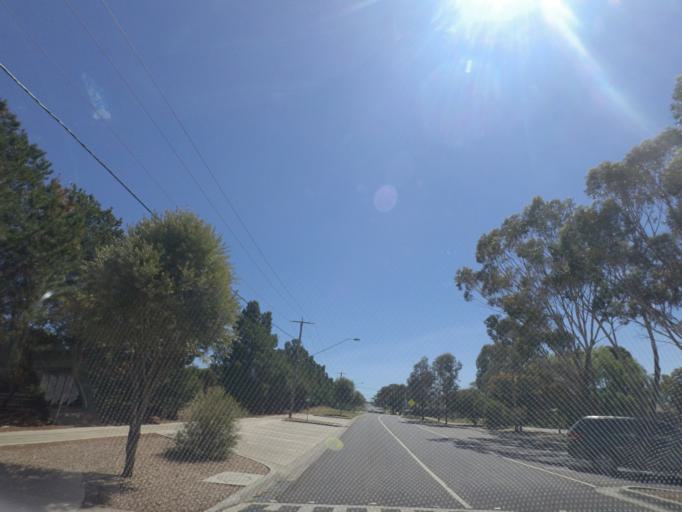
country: AU
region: Victoria
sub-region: Hume
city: Sunbury
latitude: -37.5817
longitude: 144.6929
